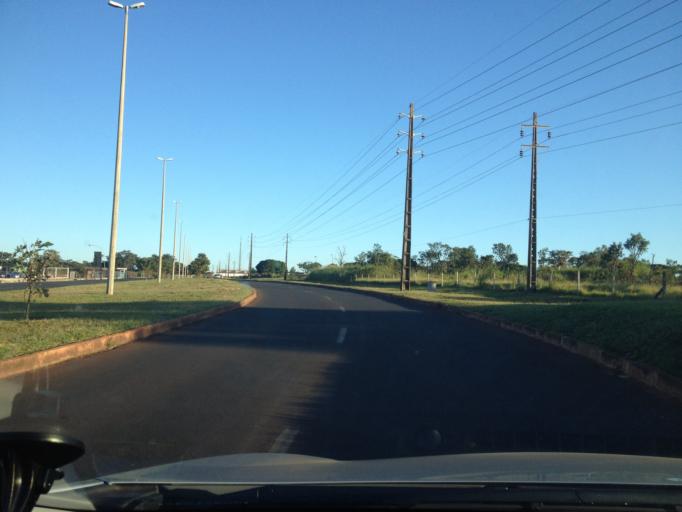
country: BR
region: Federal District
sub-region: Brasilia
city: Brasilia
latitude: -15.7663
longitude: -47.8991
